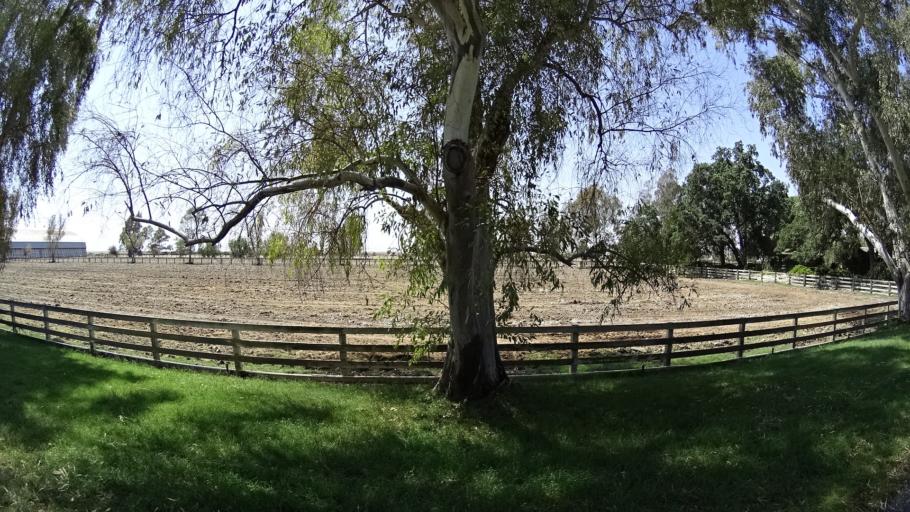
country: US
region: California
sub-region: Kings County
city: Stratford
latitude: 36.1234
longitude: -119.8873
